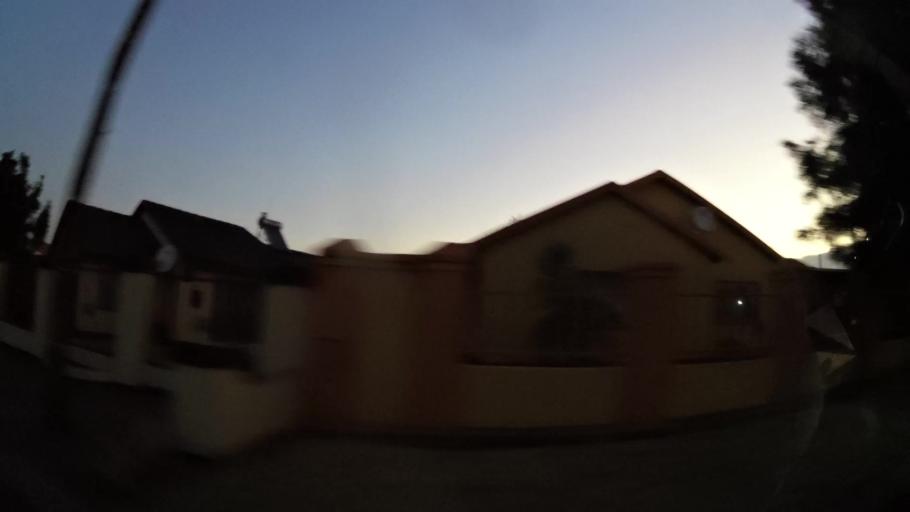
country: ZA
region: Gauteng
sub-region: West Rand District Municipality
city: Randfontein
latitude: -26.2065
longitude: 27.7056
